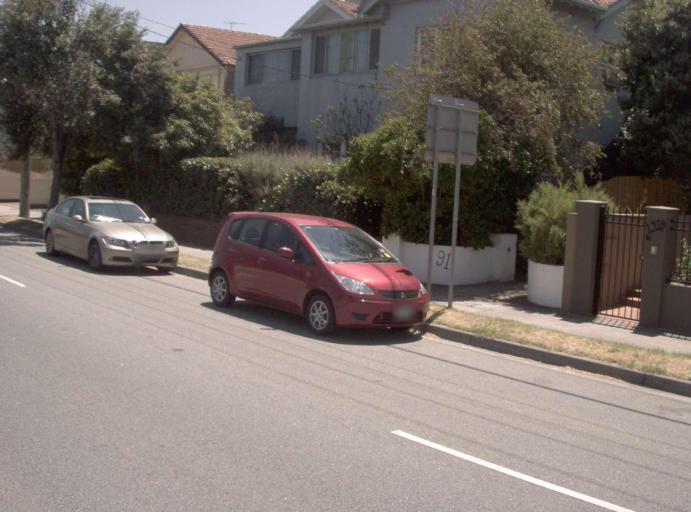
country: AU
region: Victoria
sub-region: Port Phillip
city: Elwood
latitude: -37.8887
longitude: 144.9866
